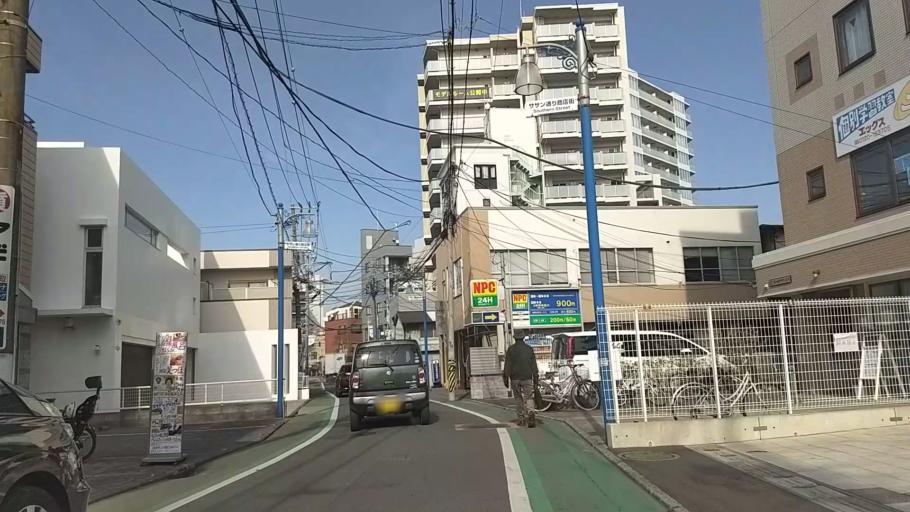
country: JP
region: Kanagawa
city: Chigasaki
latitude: 35.3283
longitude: 139.4045
